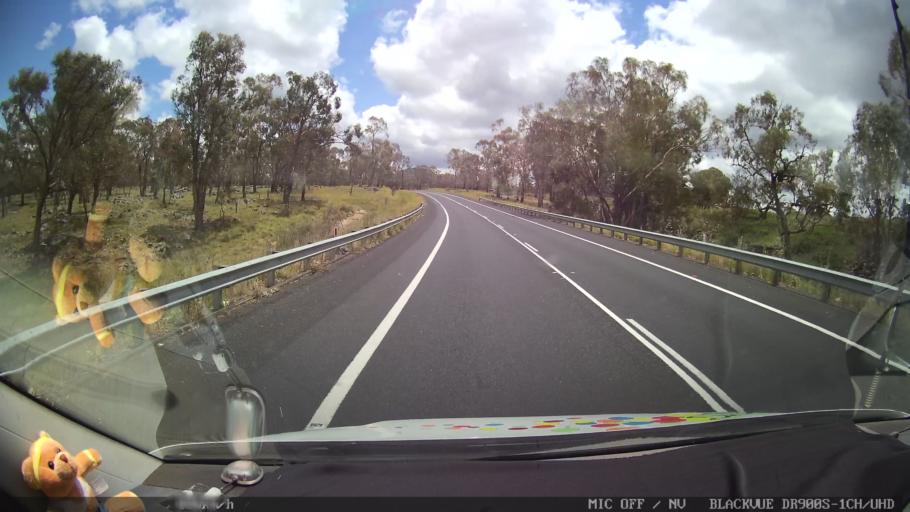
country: AU
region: New South Wales
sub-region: Glen Innes Severn
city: Glen Innes
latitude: -29.3674
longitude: 151.8980
